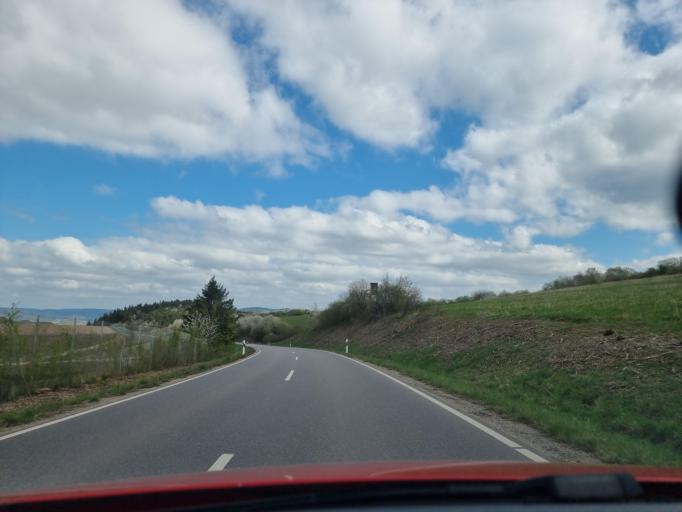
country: DE
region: Rheinland-Pfalz
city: Fell
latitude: 49.7729
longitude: 6.7603
